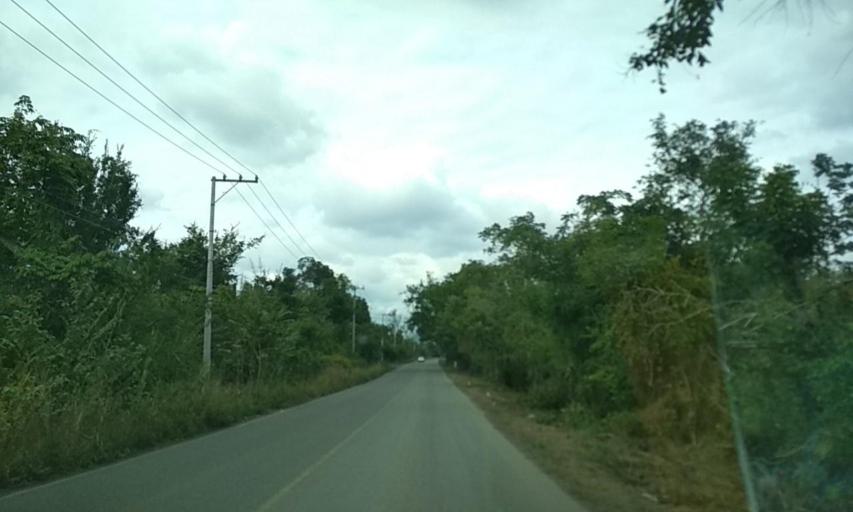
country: MX
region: Veracruz
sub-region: Papantla
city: El Chote
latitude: 20.3793
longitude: -97.3359
